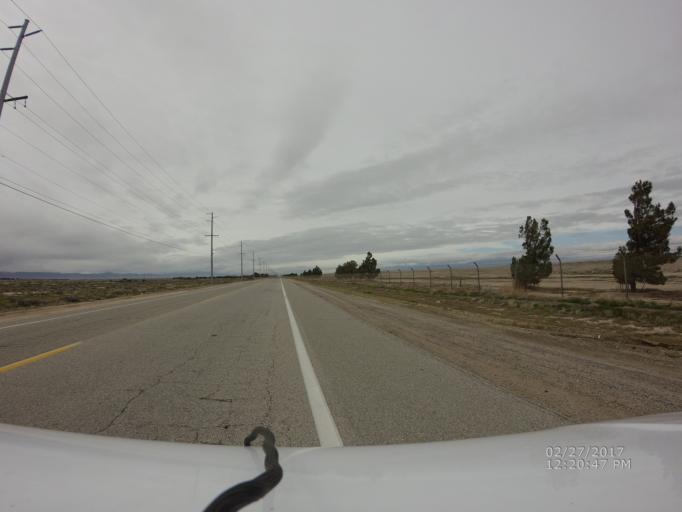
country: US
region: California
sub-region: Los Angeles County
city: Lancaster
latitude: 34.7772
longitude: -118.1500
